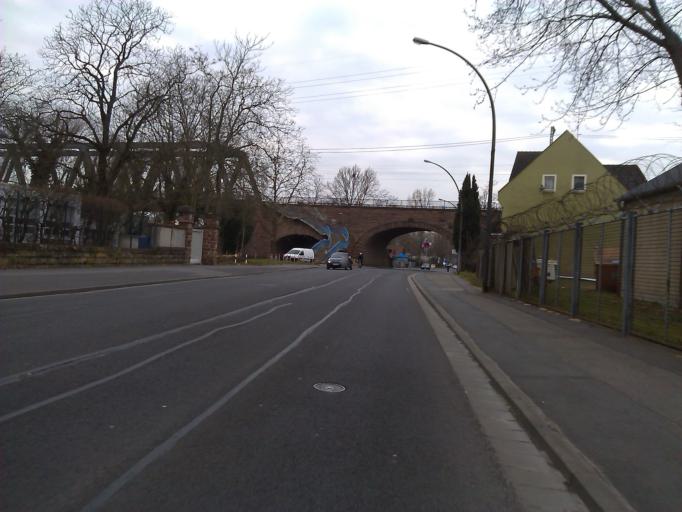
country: DE
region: Rheinland-Pfalz
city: Mainz
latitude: 50.0257
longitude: 8.2621
